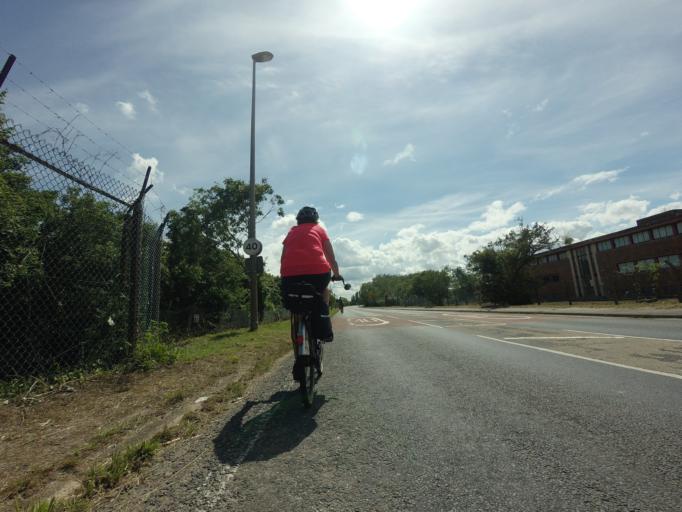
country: GB
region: England
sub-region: Medway
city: Allhallows
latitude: 51.4450
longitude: 0.6915
